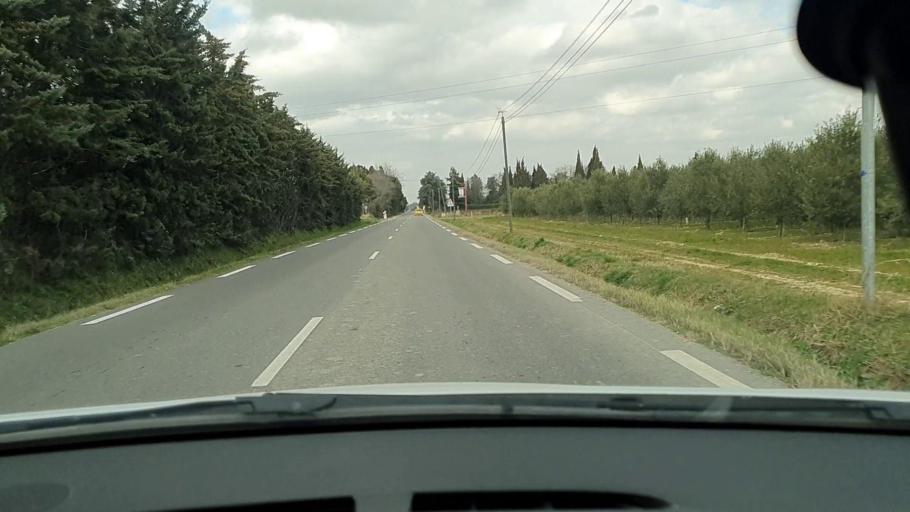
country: FR
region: Languedoc-Roussillon
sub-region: Departement du Gard
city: Meynes
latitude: 43.8916
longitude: 4.5741
